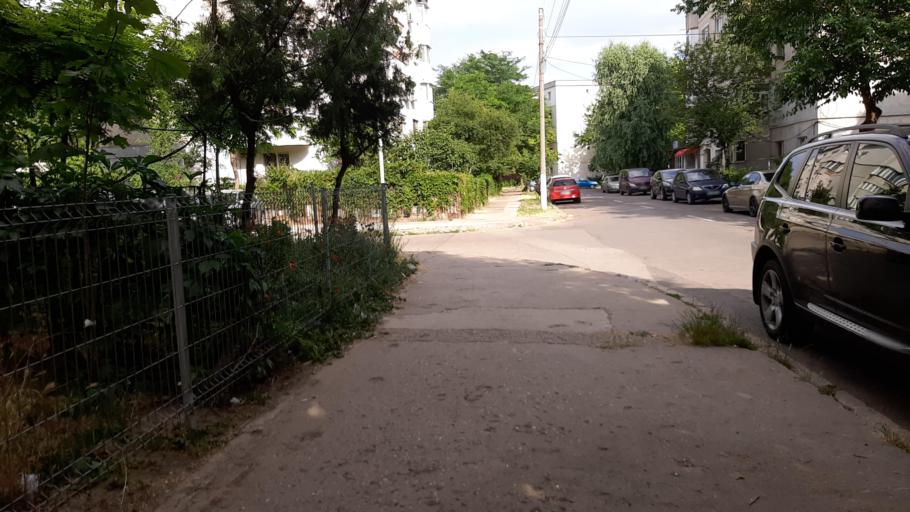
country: RO
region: Galati
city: Galati
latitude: 45.4433
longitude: 28.0260
